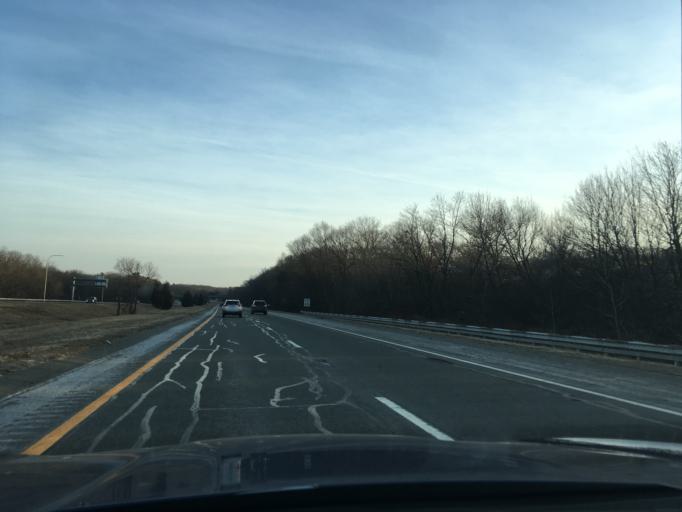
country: US
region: Rhode Island
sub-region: Providence County
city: Johnston
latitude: 41.7865
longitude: -71.5052
